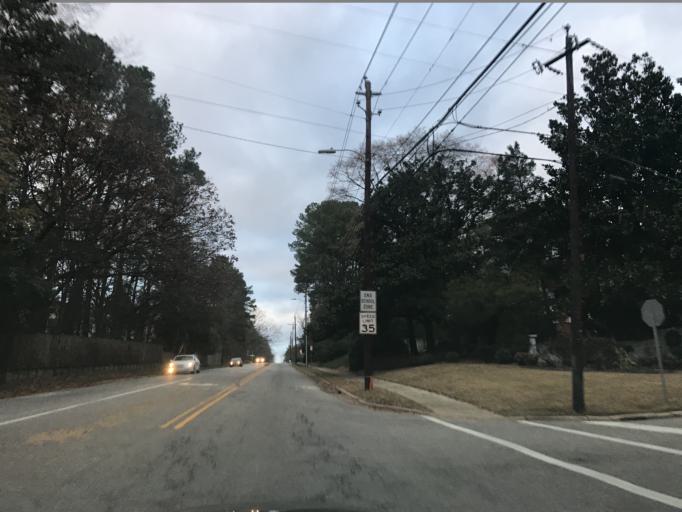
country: US
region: North Carolina
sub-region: Wake County
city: West Raleigh
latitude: 35.8289
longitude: -78.6485
